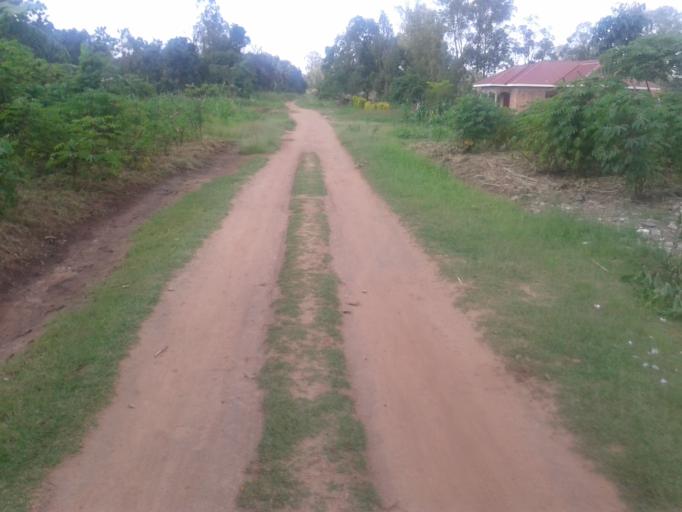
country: UG
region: Northern Region
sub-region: Gulu District
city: Gulu
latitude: 2.7921
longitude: 32.3044
